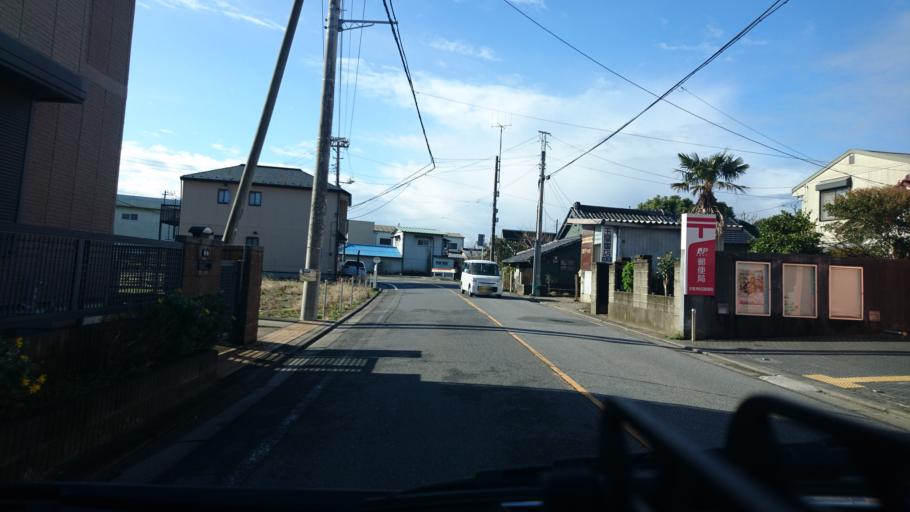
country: JP
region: Chiba
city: Kisarazu
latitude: 35.3772
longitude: 139.9221
